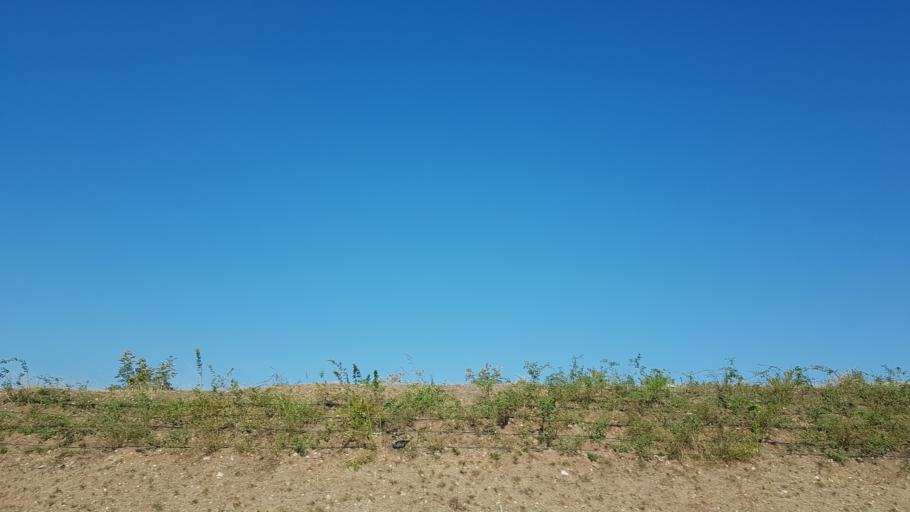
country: TR
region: Balikesir
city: Ertugrul
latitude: 39.6158
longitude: 27.7017
